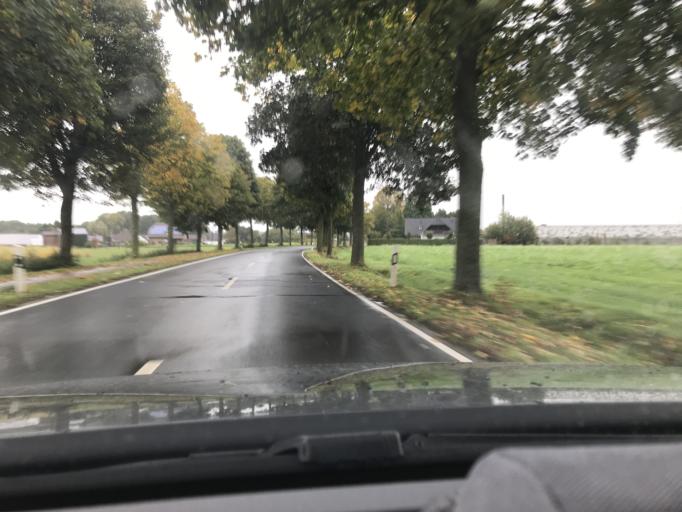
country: DE
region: North Rhine-Westphalia
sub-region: Regierungsbezirk Dusseldorf
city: Nettetal
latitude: 51.3445
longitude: 6.2912
